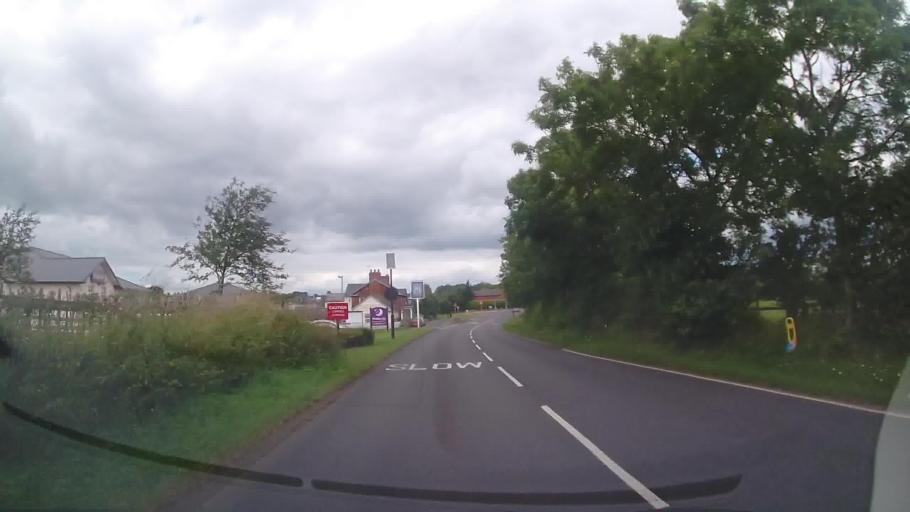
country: GB
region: England
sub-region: Shropshire
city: Clive
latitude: 52.7921
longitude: -2.7576
